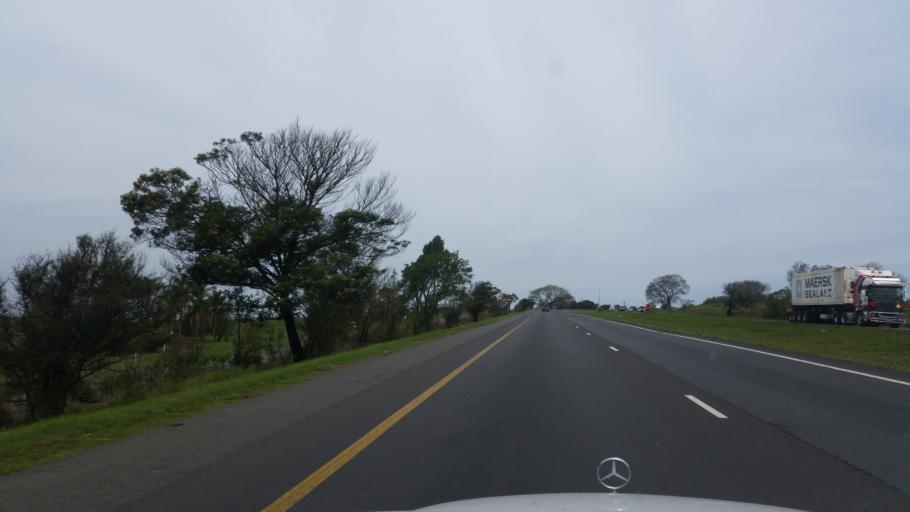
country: ZA
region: KwaZulu-Natal
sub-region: uMgungundlovu District Municipality
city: Camperdown
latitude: -29.7040
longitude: 30.4935
